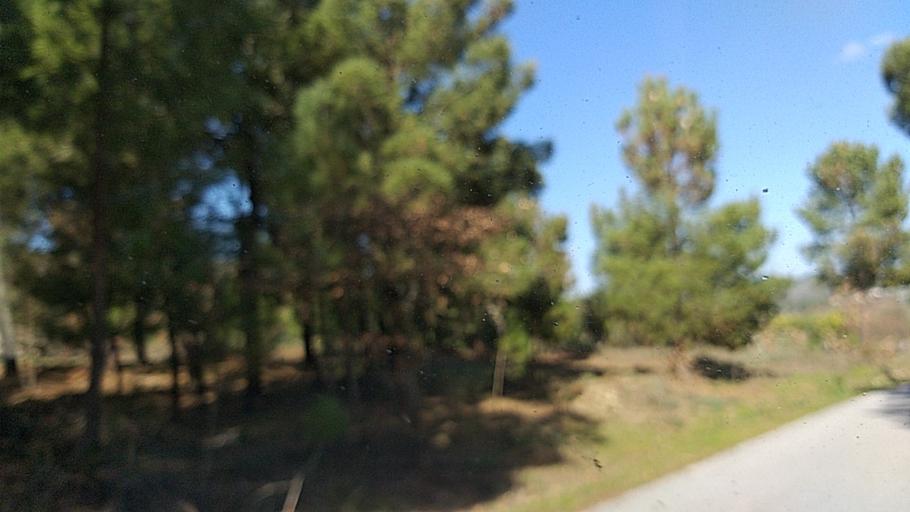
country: PT
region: Guarda
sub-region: Celorico da Beira
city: Celorico da Beira
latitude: 40.6490
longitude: -7.4263
